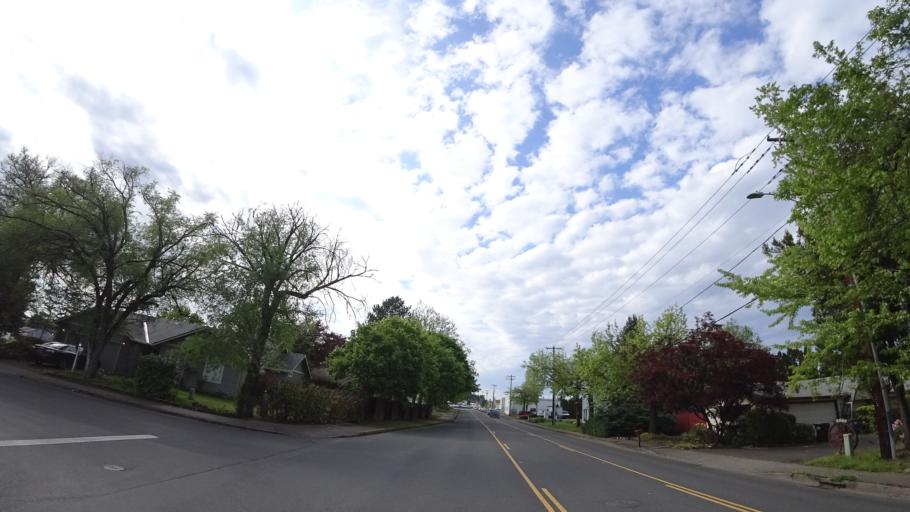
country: US
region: Oregon
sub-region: Washington County
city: Hillsboro
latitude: 45.5067
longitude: -122.9658
